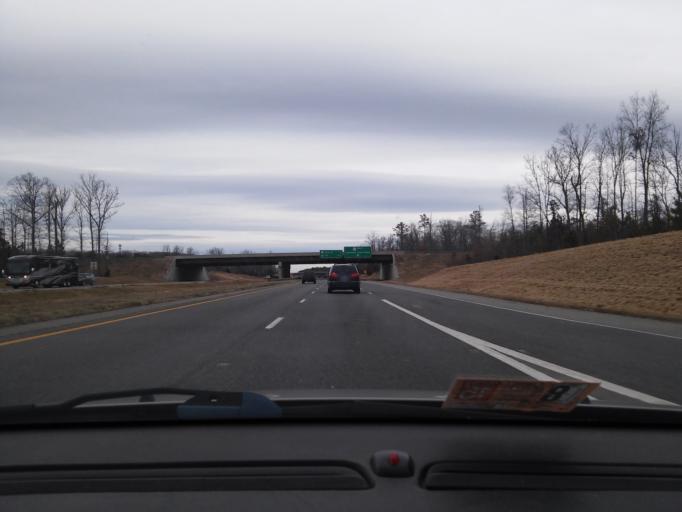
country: US
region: Virginia
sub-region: Henrico County
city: Short Pump
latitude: 37.6304
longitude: -77.6635
